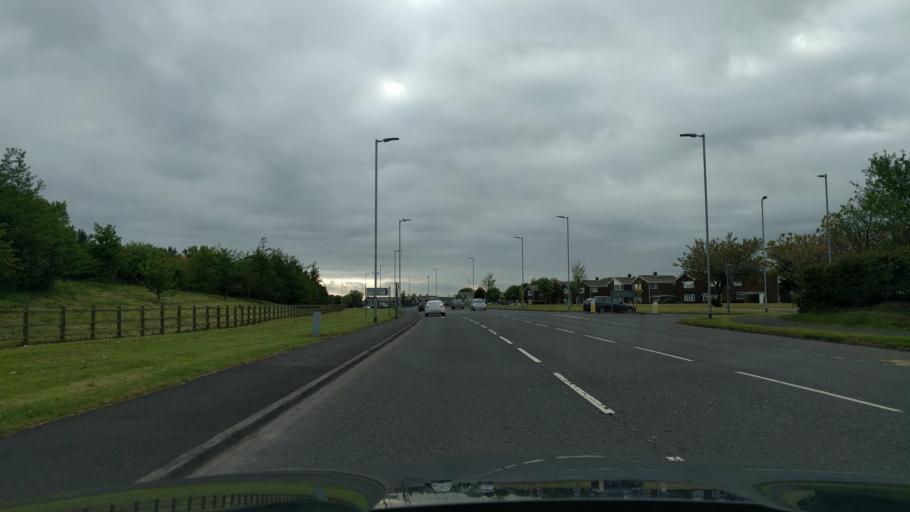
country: GB
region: England
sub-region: Northumberland
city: Newbiggin-by-the-Sea
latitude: 55.1718
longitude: -1.5377
